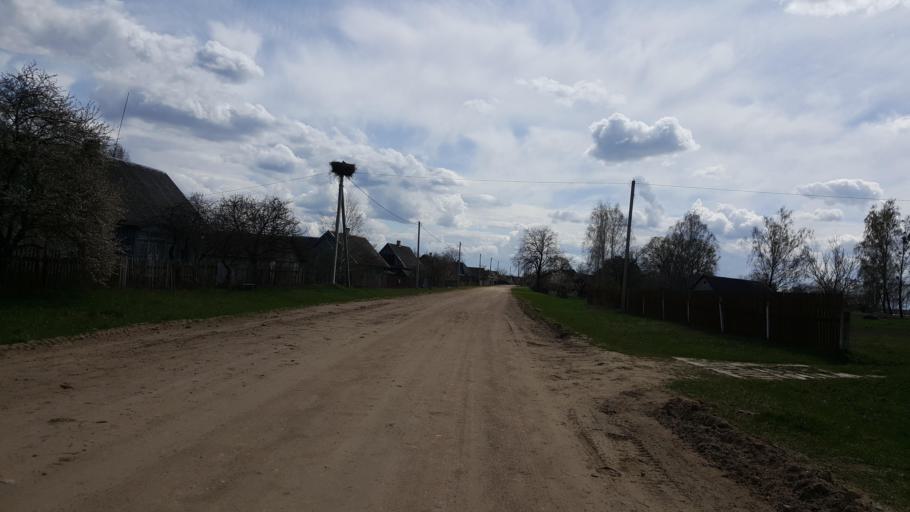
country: BY
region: Brest
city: Kamyanyets
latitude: 52.3601
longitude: 23.7316
